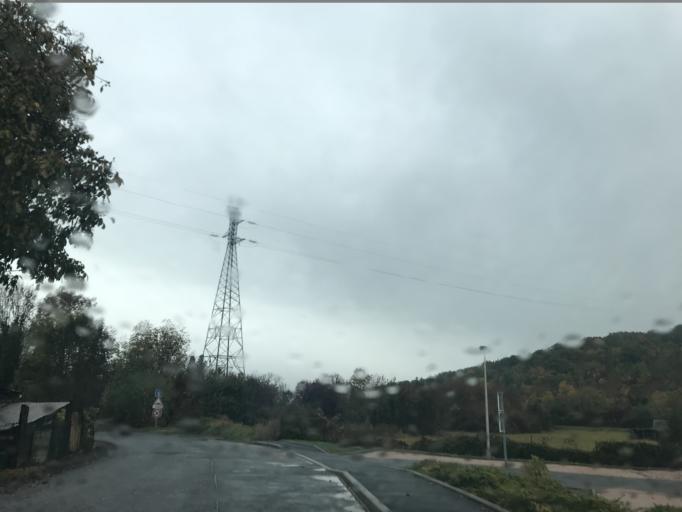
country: FR
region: Auvergne
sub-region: Departement du Puy-de-Dome
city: Durtol
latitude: 45.7983
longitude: 3.0553
